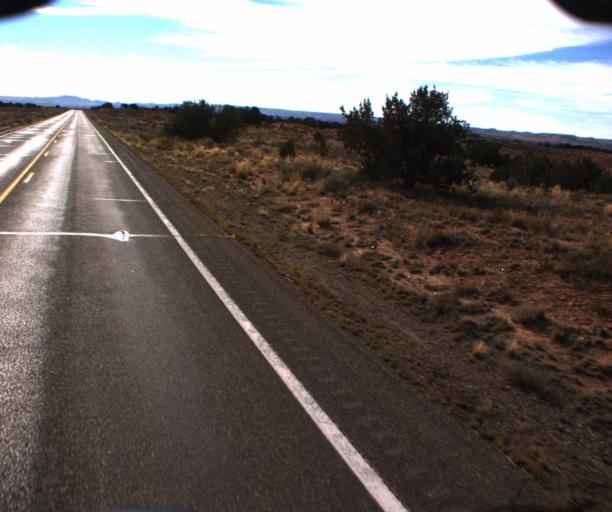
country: US
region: Arizona
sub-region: Coconino County
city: Kaibito
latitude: 36.6684
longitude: -111.2545
